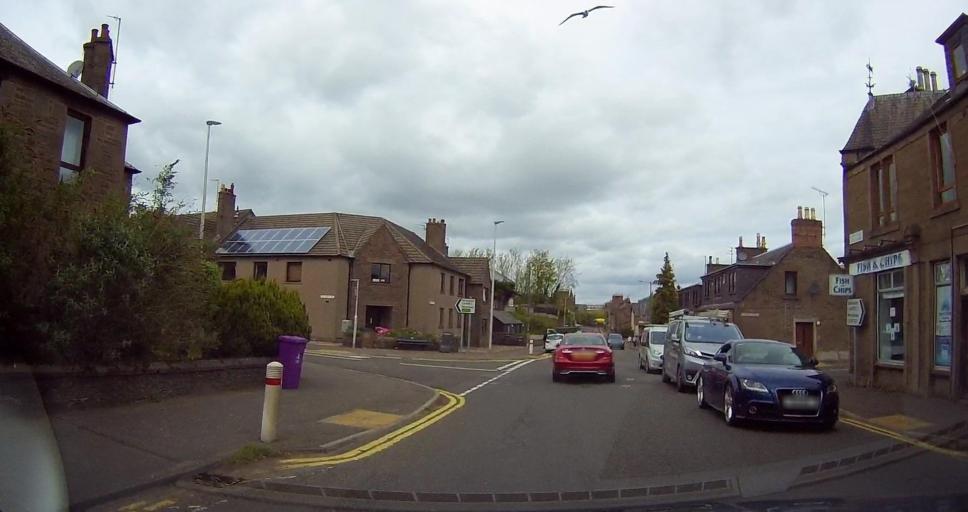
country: GB
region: Scotland
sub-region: Angus
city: Forfar
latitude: 56.6479
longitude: -2.8829
